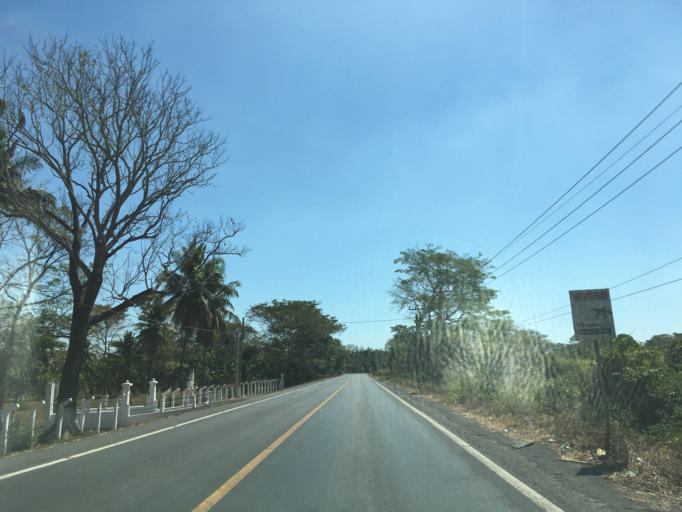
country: GT
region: Escuintla
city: Puerto San Jose
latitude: 13.9785
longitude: -90.8832
